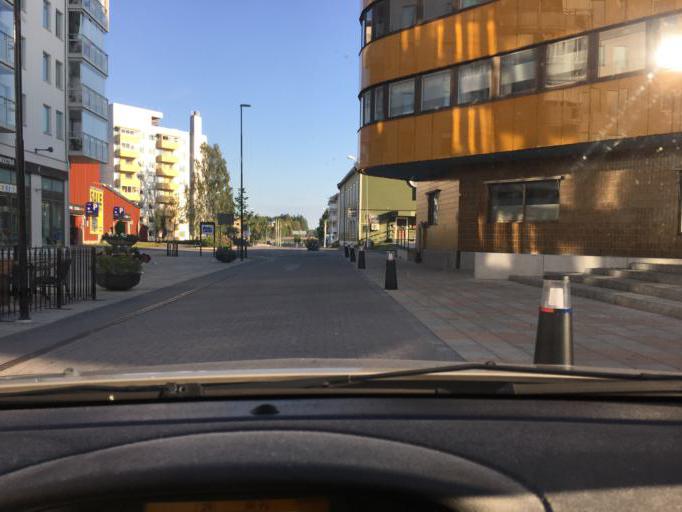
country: SE
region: Norrbotten
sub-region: Bodens Kommun
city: Boden
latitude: 65.8249
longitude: 21.6888
